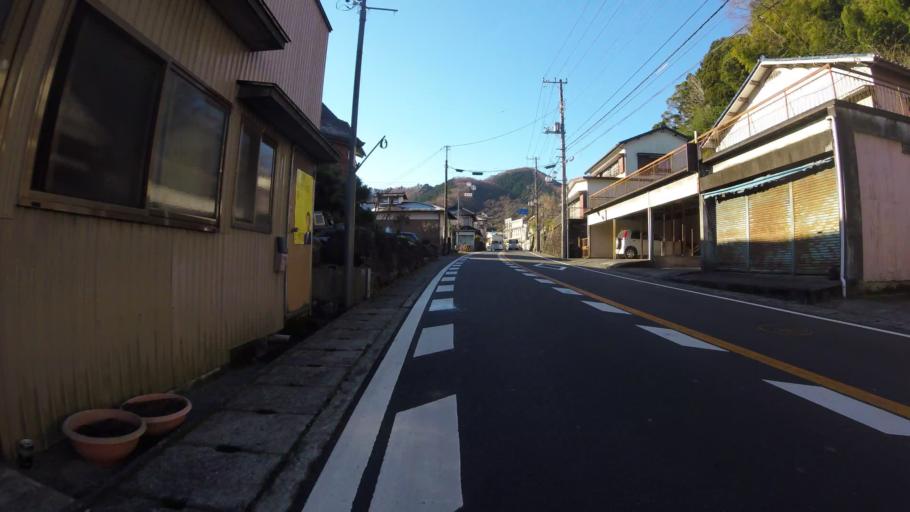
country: JP
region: Shizuoka
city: Heda
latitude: 34.8910
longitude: 138.9293
